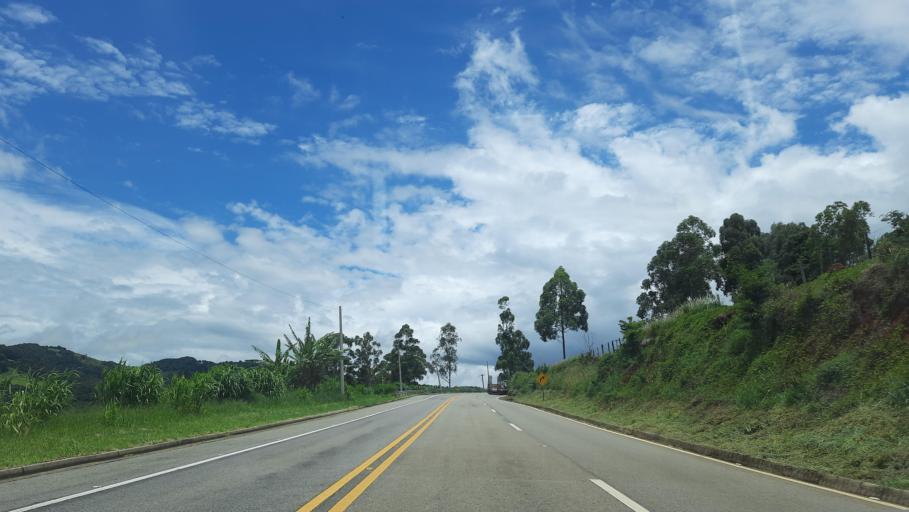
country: BR
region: Sao Paulo
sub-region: Vargem Grande Do Sul
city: Vargem Grande do Sul
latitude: -21.8289
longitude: -46.7681
